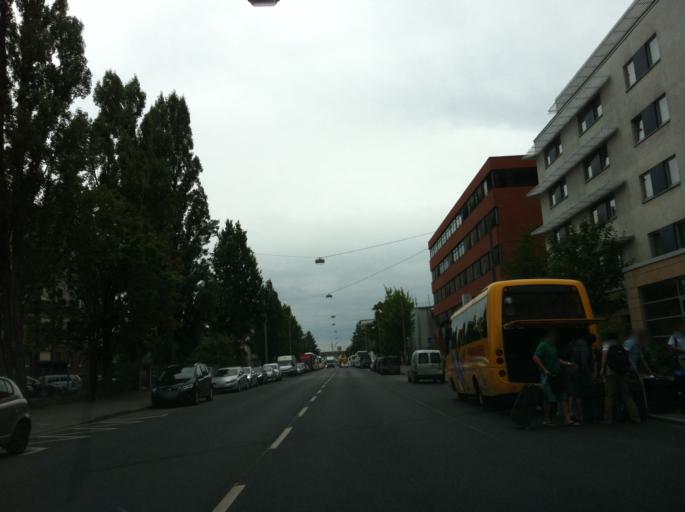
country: DE
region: Hesse
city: Niederrad
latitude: 50.0974
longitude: 8.6463
